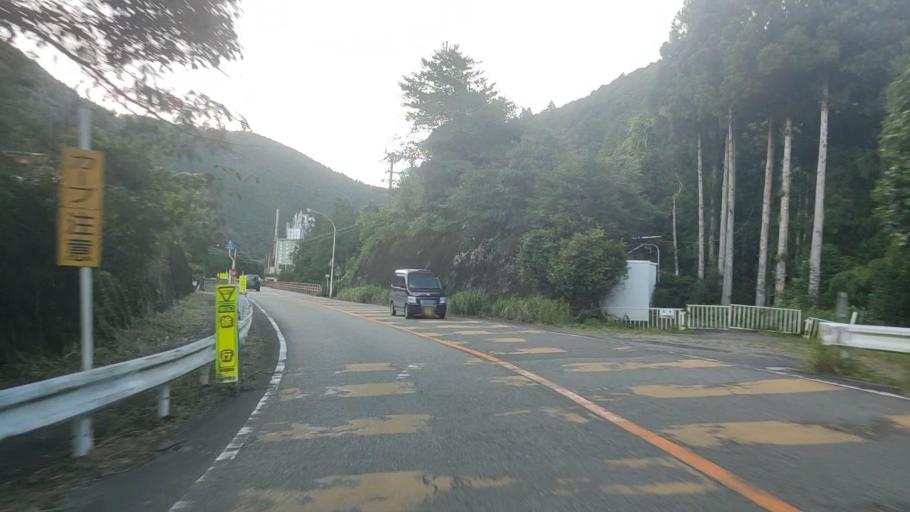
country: JP
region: Wakayama
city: Tanabe
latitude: 33.8153
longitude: 135.5533
